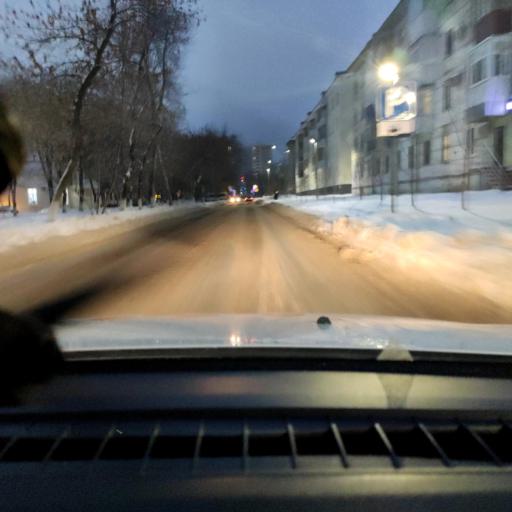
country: RU
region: Samara
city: Novokuybyshevsk
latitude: 53.0969
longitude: 49.9547
